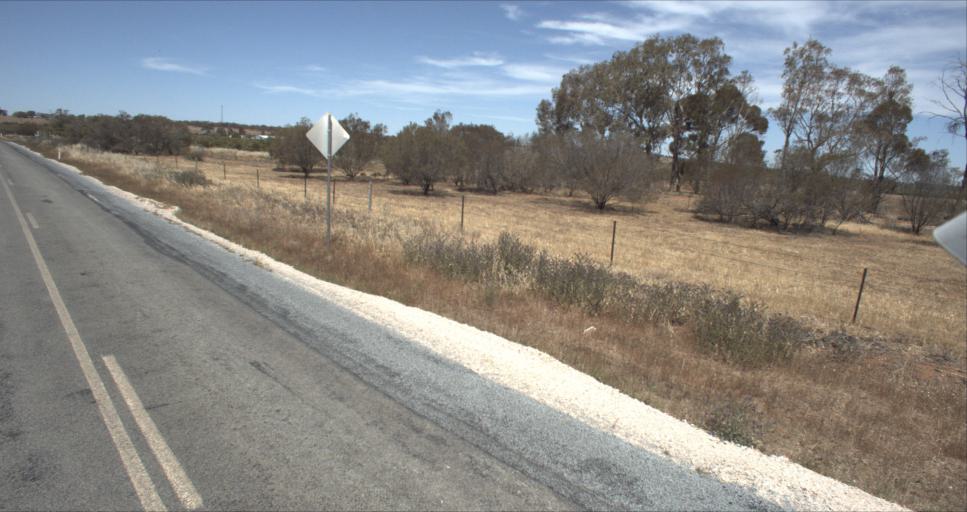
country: AU
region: New South Wales
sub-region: Leeton
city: Leeton
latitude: -34.5875
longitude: 146.4359
